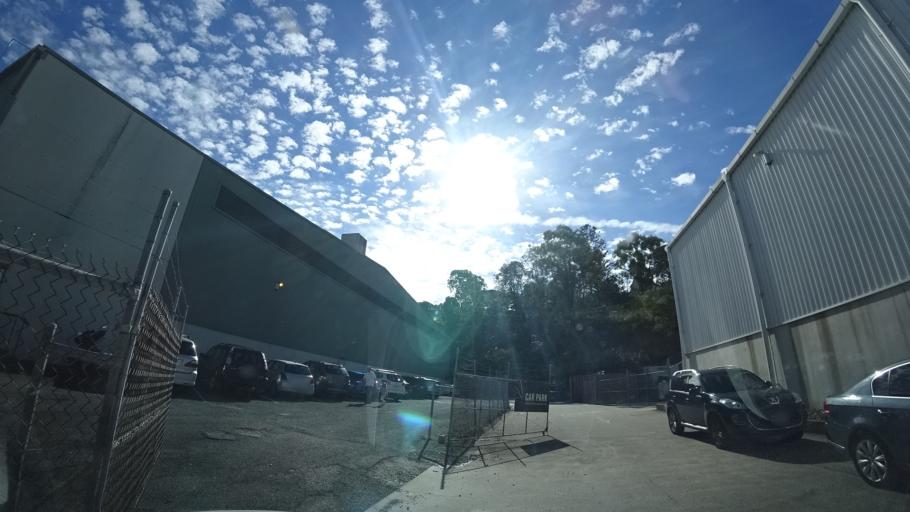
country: AU
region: Queensland
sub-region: Brisbane
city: Grange
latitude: -27.4273
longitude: 153.0066
